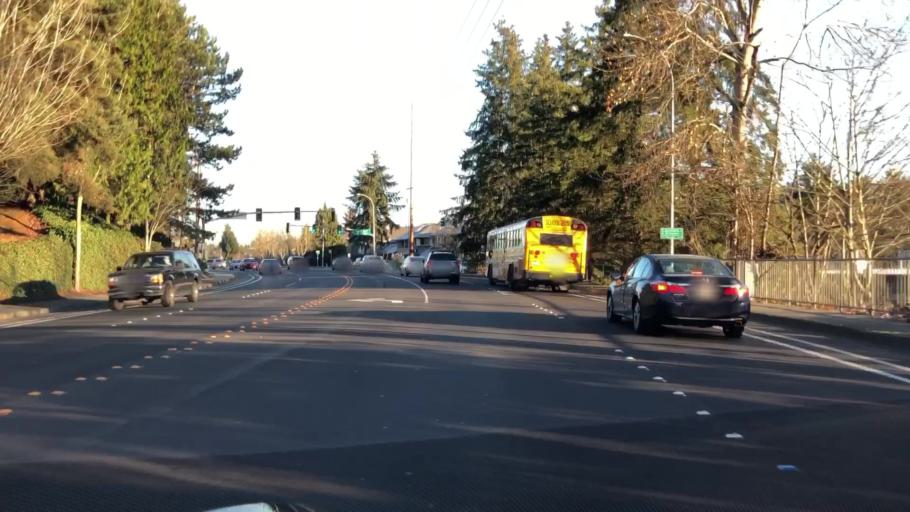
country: US
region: Washington
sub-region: King County
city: Newport
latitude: 47.5865
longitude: -122.1646
